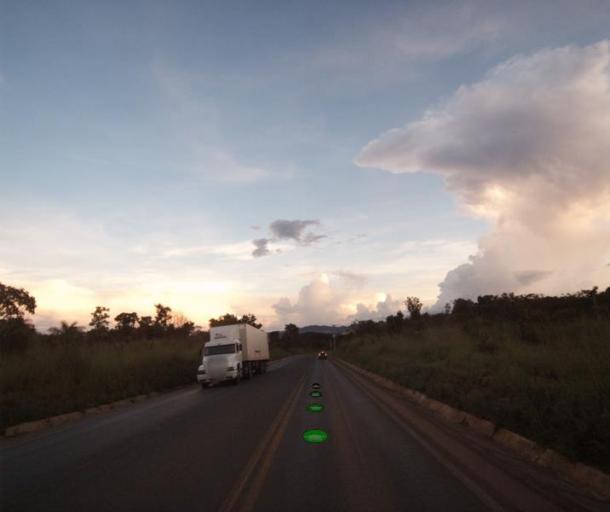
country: BR
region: Goias
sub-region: Uruacu
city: Uruacu
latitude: -14.4809
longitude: -49.1542
